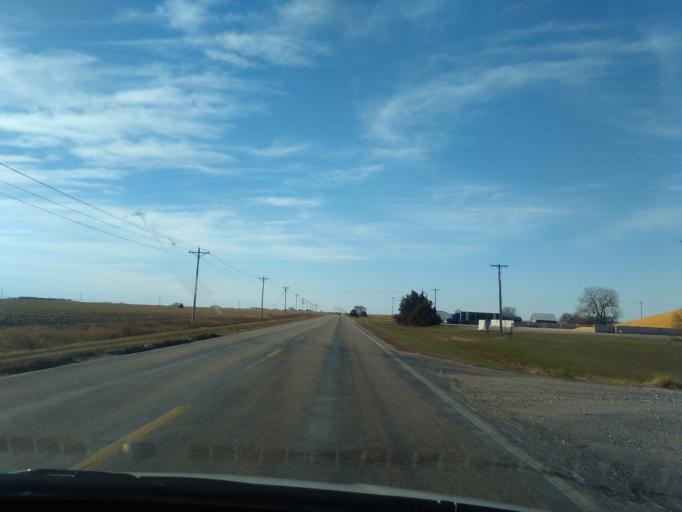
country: US
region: Nebraska
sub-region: Clay County
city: Harvard
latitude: 40.6115
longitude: -98.0998
